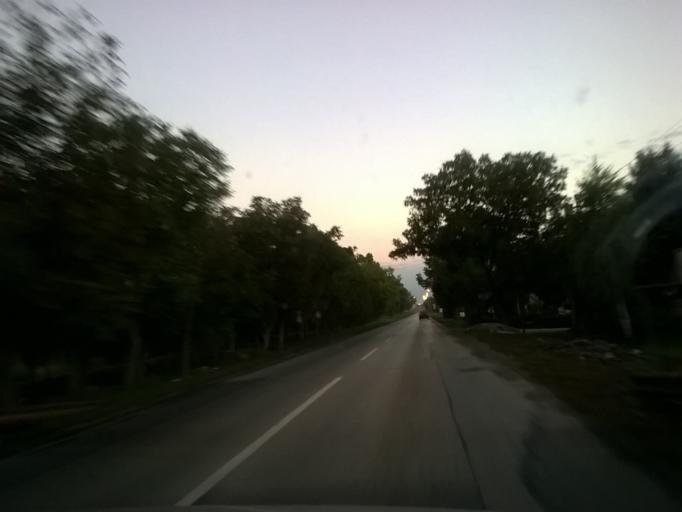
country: RS
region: Autonomna Pokrajina Vojvodina
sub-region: Juznobanatski Okrug
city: Pancevo
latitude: 44.8957
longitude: 20.6312
